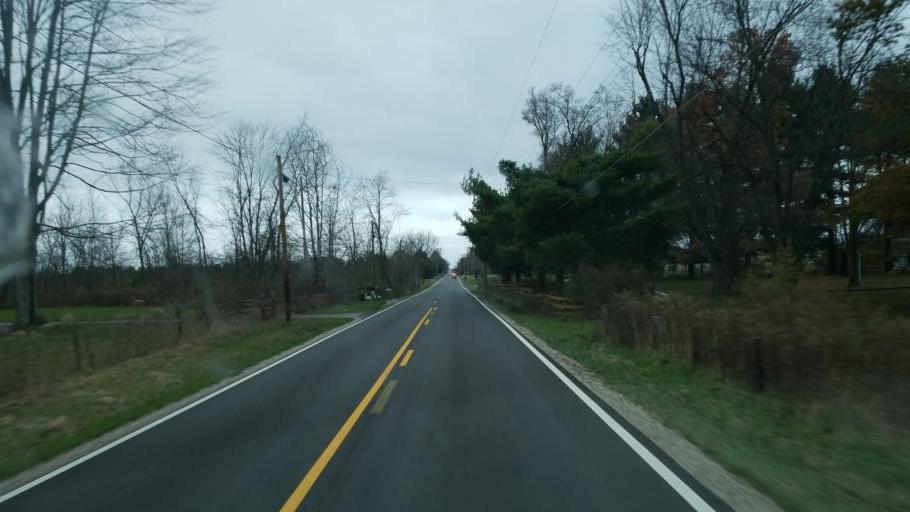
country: US
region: Ohio
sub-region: Delaware County
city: Sunbury
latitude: 40.2990
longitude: -82.9106
